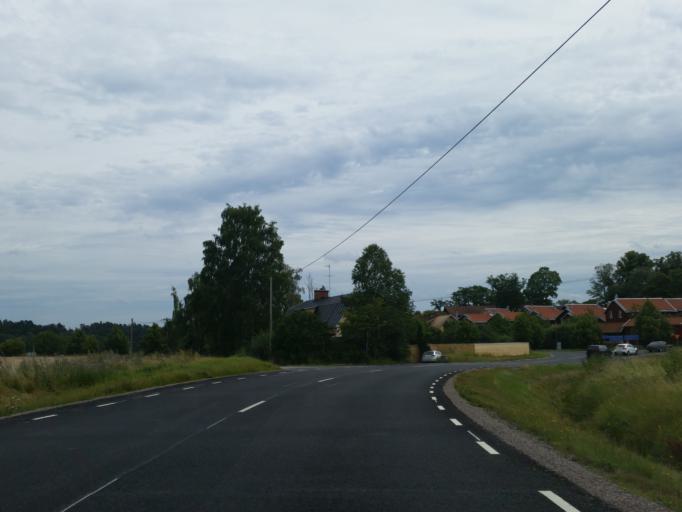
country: SE
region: Soedermanland
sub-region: Strangnas Kommun
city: Mariefred
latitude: 59.2554
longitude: 17.1799
